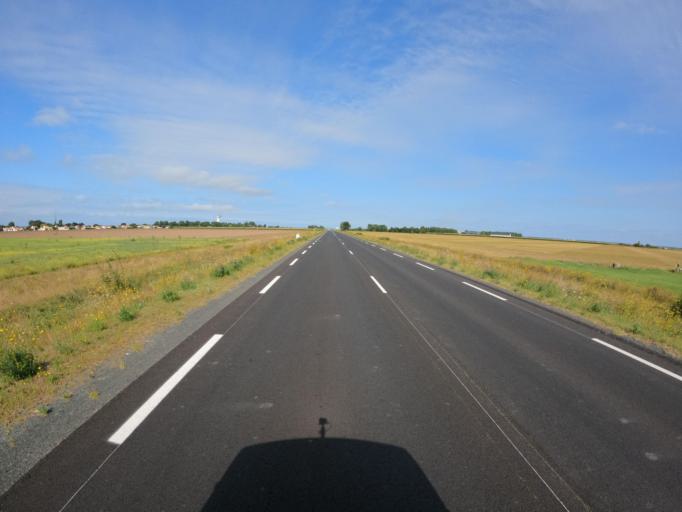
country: FR
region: Pays de la Loire
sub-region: Departement de la Vendee
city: Angles
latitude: 46.3442
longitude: -1.3063
